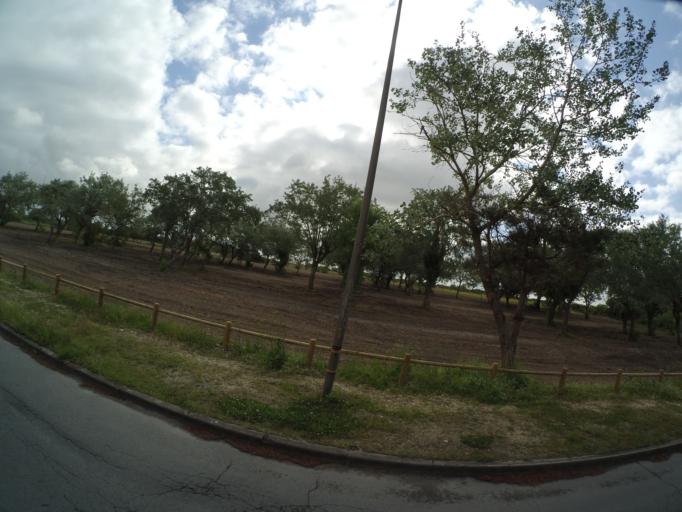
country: FR
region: Poitou-Charentes
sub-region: Departement de la Charente-Maritime
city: Angoulins
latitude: 46.1144
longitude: -1.1232
